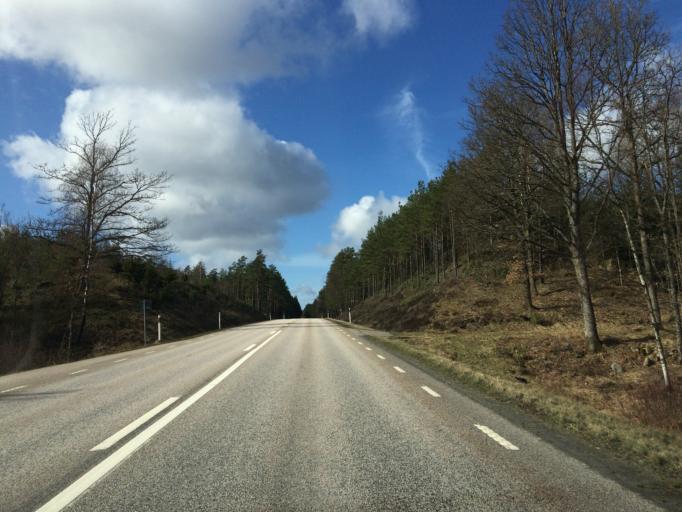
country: SE
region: Halland
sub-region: Laholms Kommun
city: Knared
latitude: 56.4890
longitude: 13.4145
